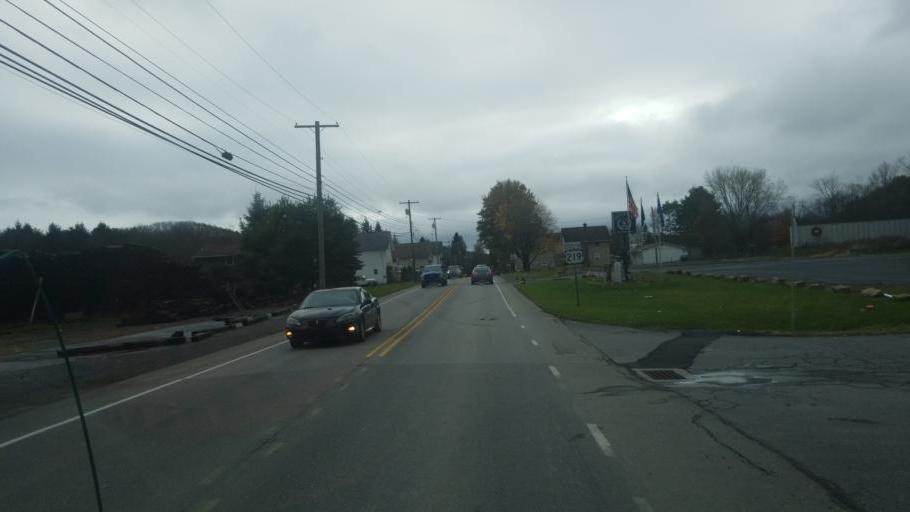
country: US
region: Pennsylvania
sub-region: Jefferson County
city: Brockway
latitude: 41.2604
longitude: -78.7259
